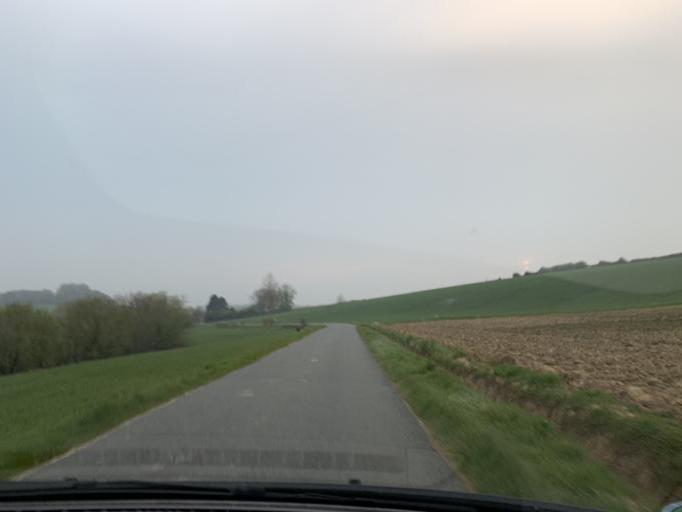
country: FR
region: Nord-Pas-de-Calais
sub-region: Departement du Pas-de-Calais
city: Wimille
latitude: 50.7624
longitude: 1.6526
